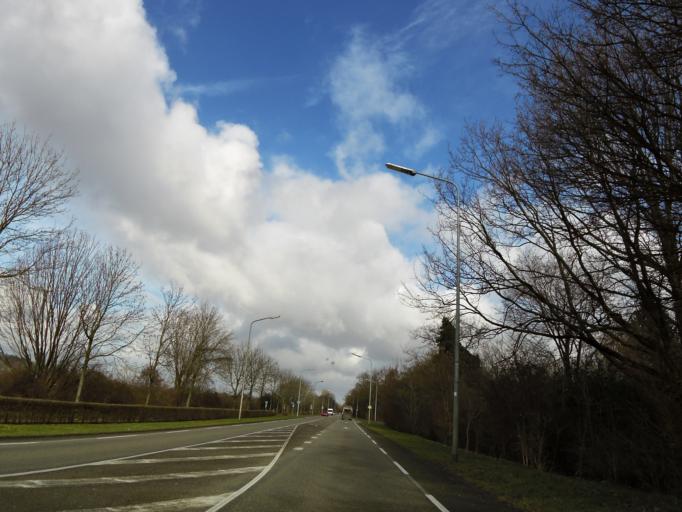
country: NL
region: Limburg
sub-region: Gemeente Maastricht
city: Maastricht
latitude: 50.8256
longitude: 5.7039
